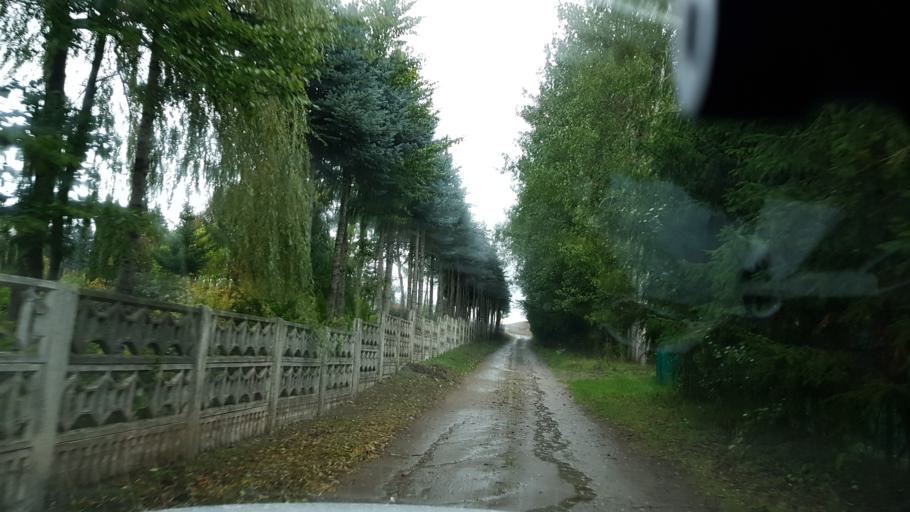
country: PL
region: West Pomeranian Voivodeship
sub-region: Powiat goleniowski
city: Przybiernow
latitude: 53.7476
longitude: 14.7687
